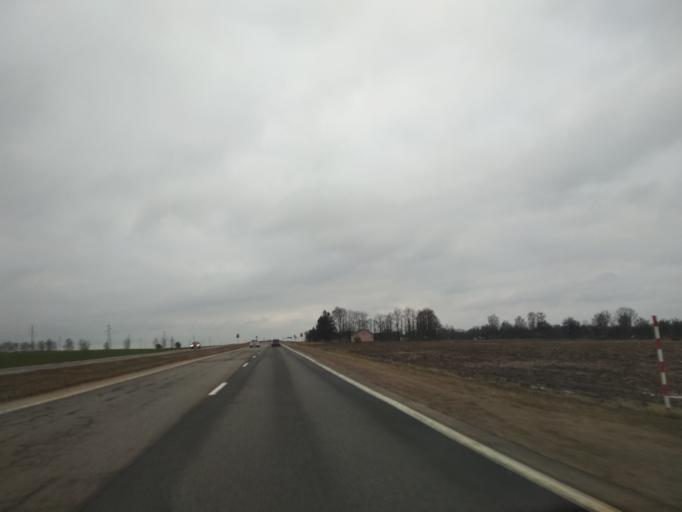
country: BY
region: Minsk
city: Mar''ina Horka
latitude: 53.5908
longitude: 28.1020
